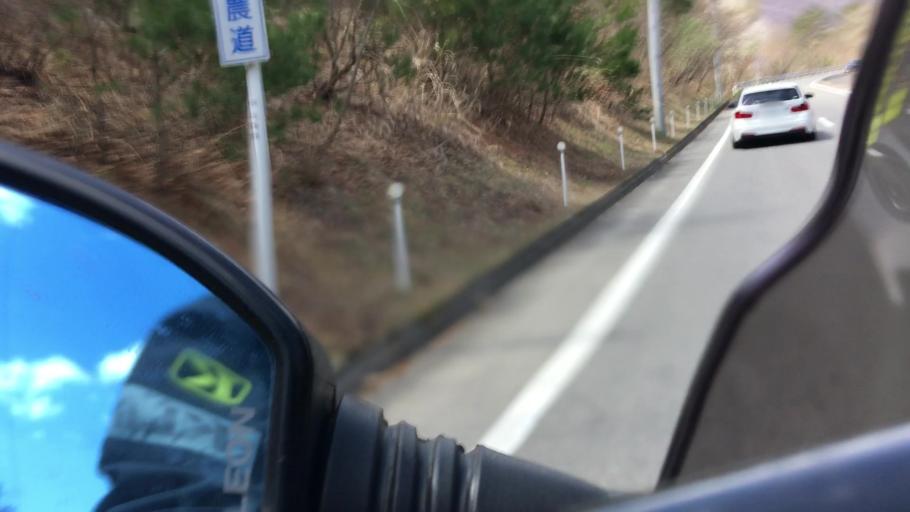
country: JP
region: Yamanashi
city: Nirasaki
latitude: 35.7791
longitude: 138.3294
